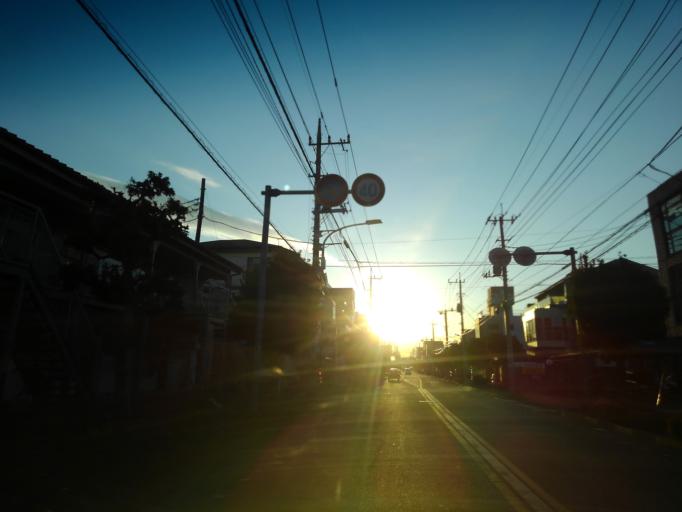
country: JP
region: Saitama
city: Tokorozawa
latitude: 35.7974
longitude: 139.5128
